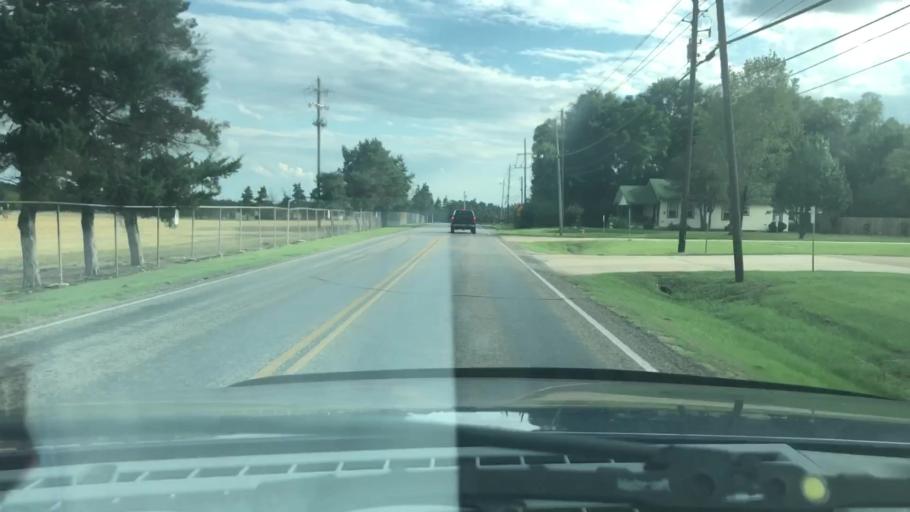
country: US
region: Texas
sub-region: Bowie County
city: Texarkana
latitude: 33.3954
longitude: -94.0647
